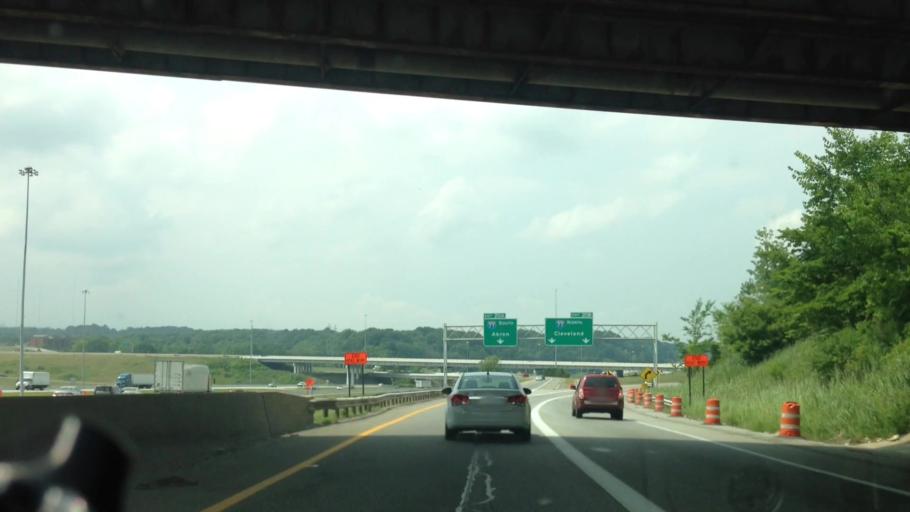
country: US
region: Ohio
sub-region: Cuyahoga County
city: Garfield Heights
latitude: 41.4077
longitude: -81.6401
